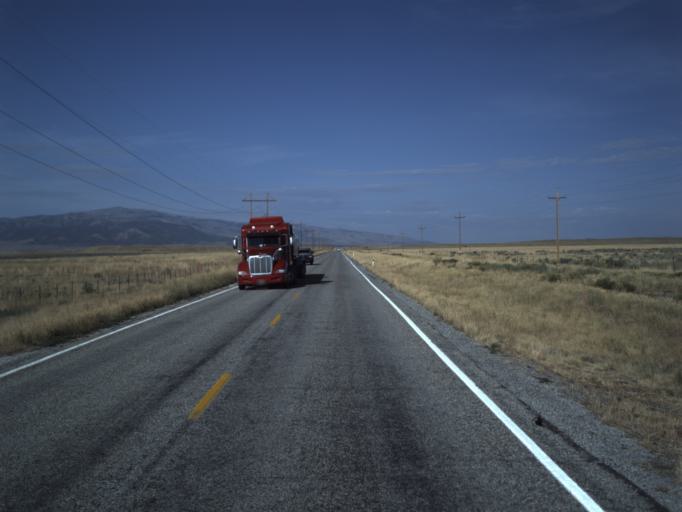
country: US
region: Idaho
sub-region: Oneida County
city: Malad City
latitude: 41.9656
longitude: -113.0257
